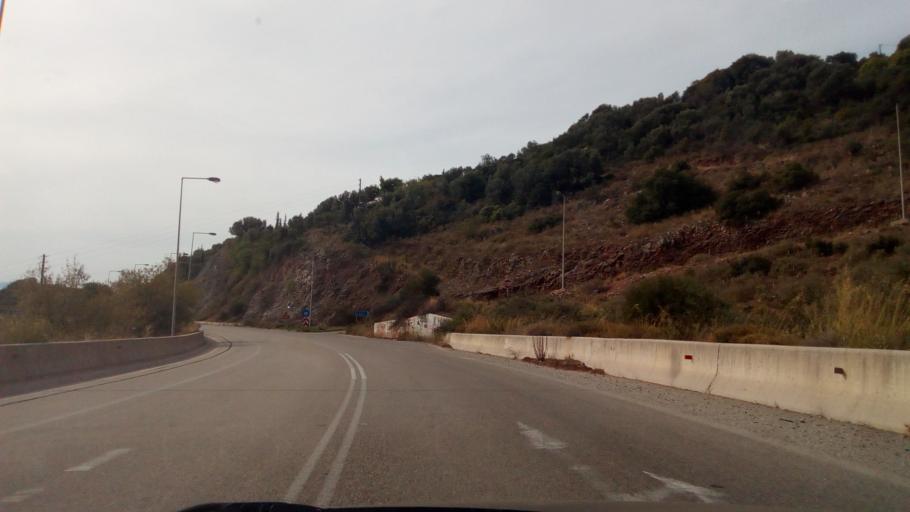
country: GR
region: West Greece
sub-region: Nomos Aitolias kai Akarnanias
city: Nafpaktos
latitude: 38.4124
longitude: 21.8400
